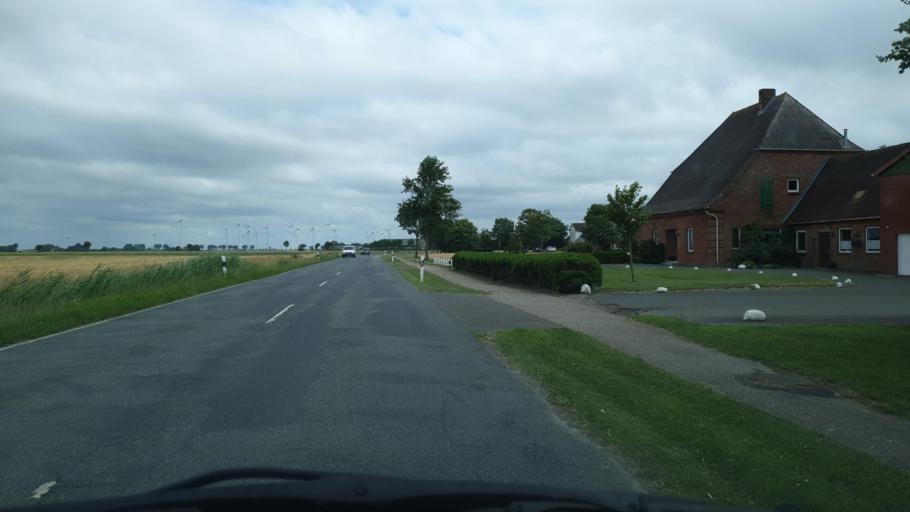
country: DE
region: Schleswig-Holstein
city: Friedrichskoog
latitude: 54.0211
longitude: 8.8779
